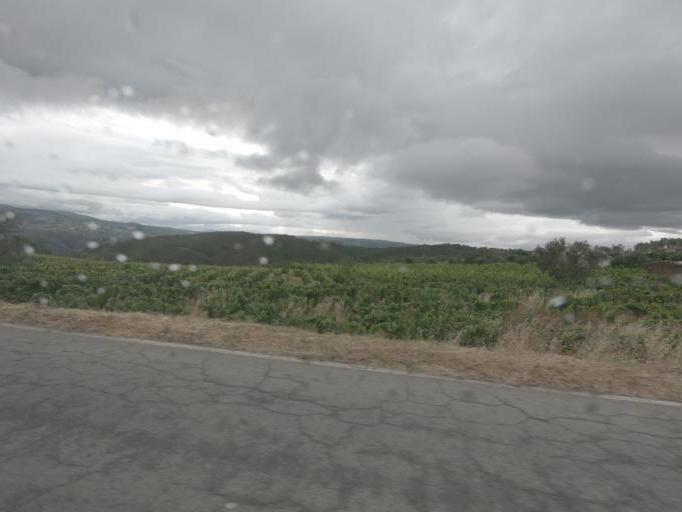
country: PT
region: Vila Real
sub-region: Sabrosa
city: Sabrosa
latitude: 41.2616
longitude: -7.5019
